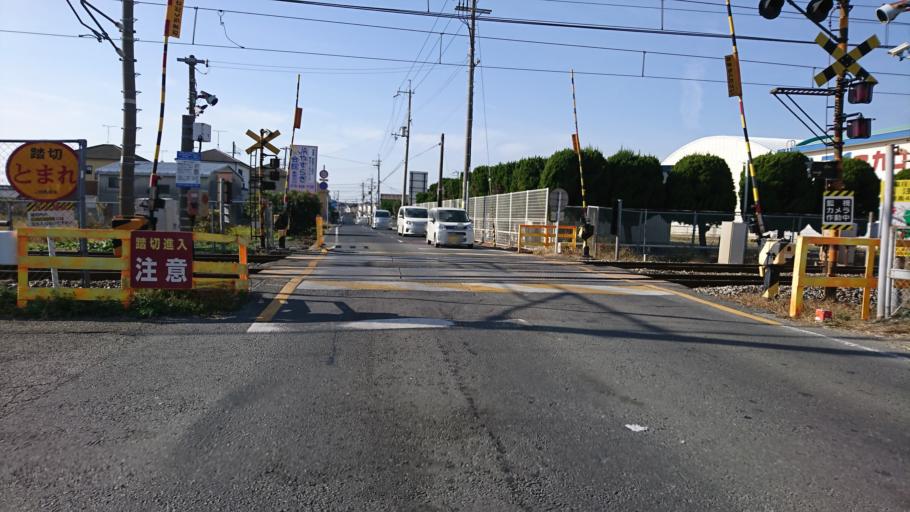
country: JP
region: Hyogo
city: Kakogawacho-honmachi
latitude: 34.7362
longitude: 134.8780
